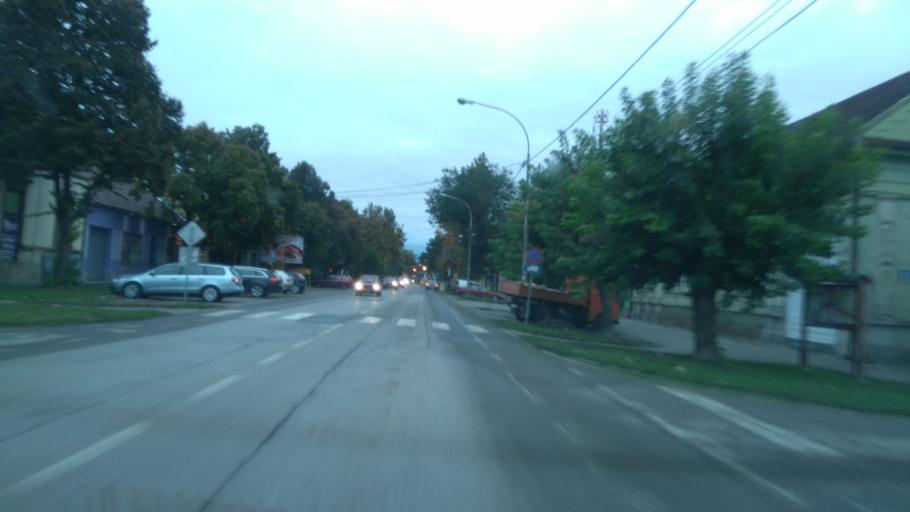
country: RS
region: Autonomna Pokrajina Vojvodina
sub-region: Juznobacki Okrug
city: Zabalj
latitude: 45.3752
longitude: 20.0624
